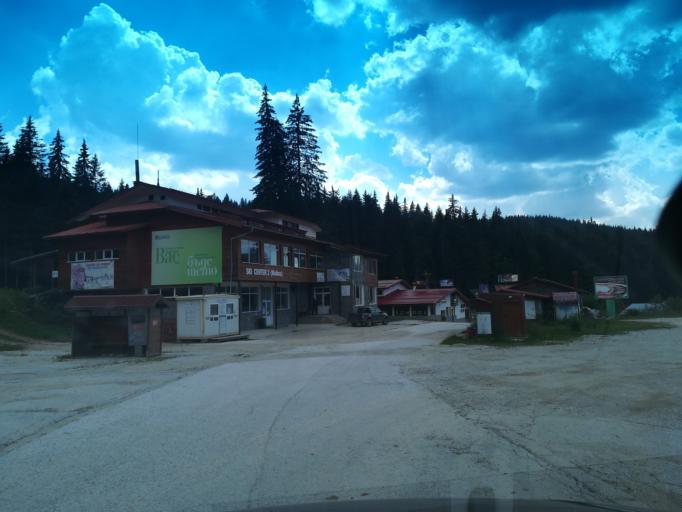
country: BG
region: Smolyan
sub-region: Obshtina Smolyan
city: Smolyan
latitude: 41.6555
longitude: 24.6816
